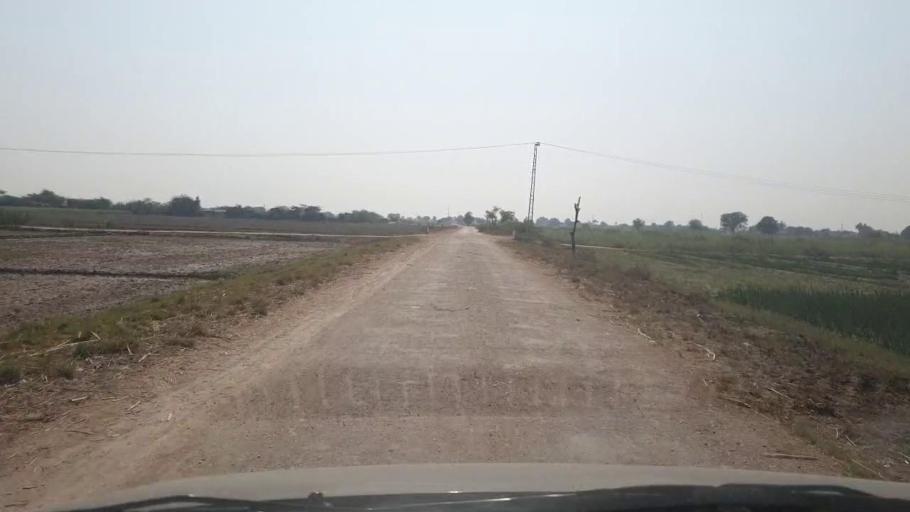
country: PK
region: Sindh
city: Mirwah Gorchani
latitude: 25.3121
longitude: 69.1599
